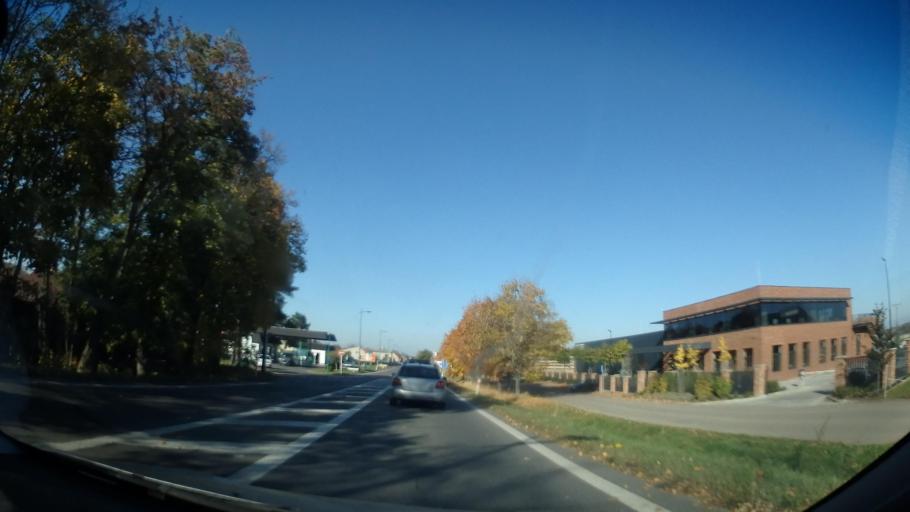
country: CZ
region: Pardubicky
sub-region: Okres Chrudim
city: Slatinany
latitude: 49.9100
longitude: 15.8193
